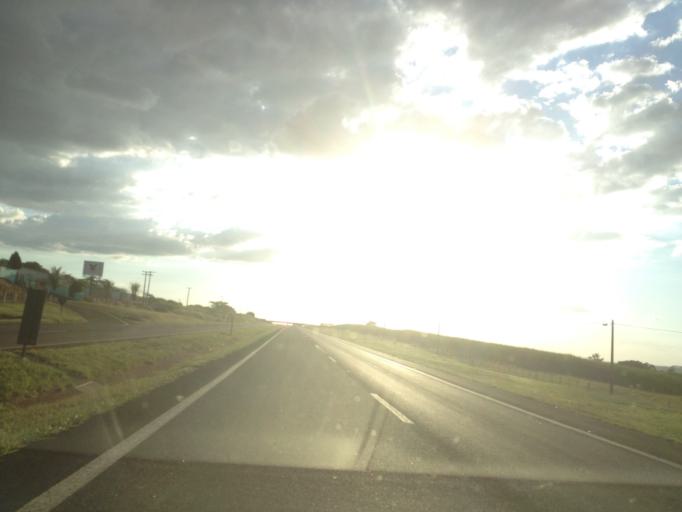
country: BR
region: Sao Paulo
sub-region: Jau
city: Jau
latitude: -22.2702
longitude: -48.4797
